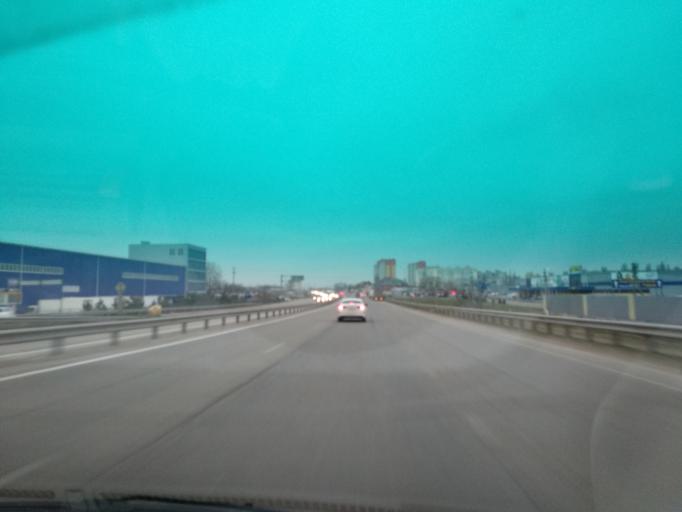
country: RU
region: Krasnodarskiy
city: Pashkovskiy
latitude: 45.0400
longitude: 39.1281
